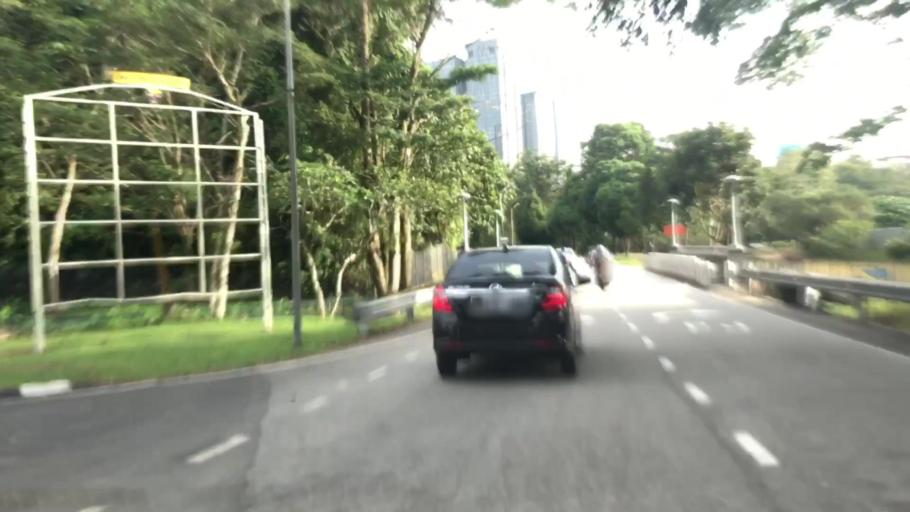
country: MY
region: Kuala Lumpur
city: Kuala Lumpur
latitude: 3.1213
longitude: 101.6606
